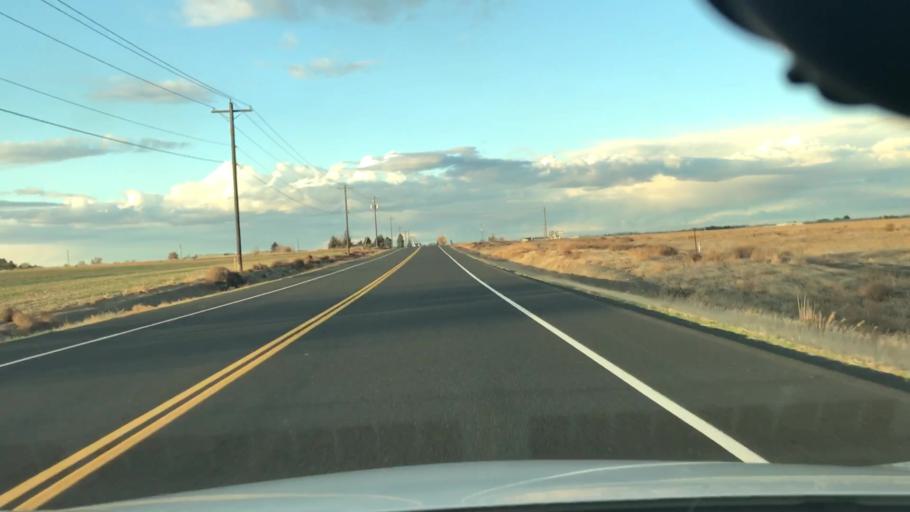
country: US
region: Washington
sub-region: Grant County
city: Moses Lake
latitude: 47.1118
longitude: -119.2360
